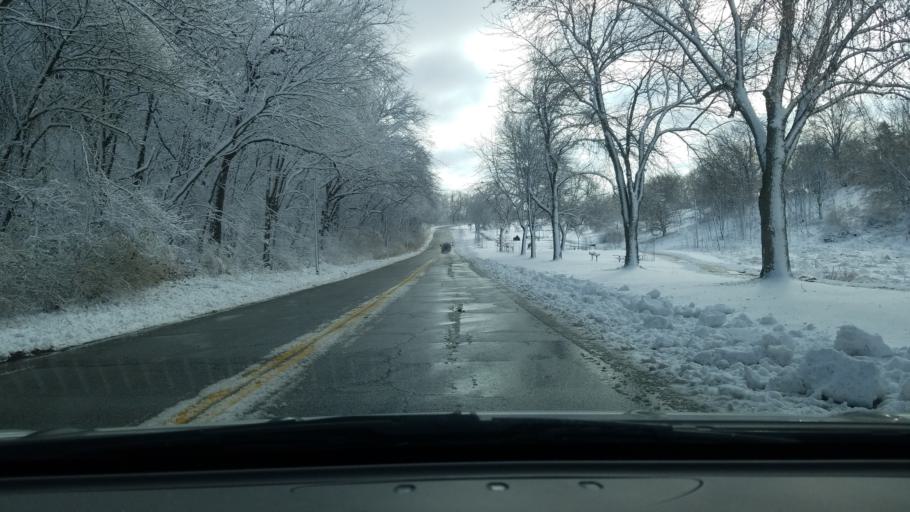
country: US
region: Nebraska
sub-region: Douglas County
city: Omaha
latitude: 41.2187
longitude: -95.9359
